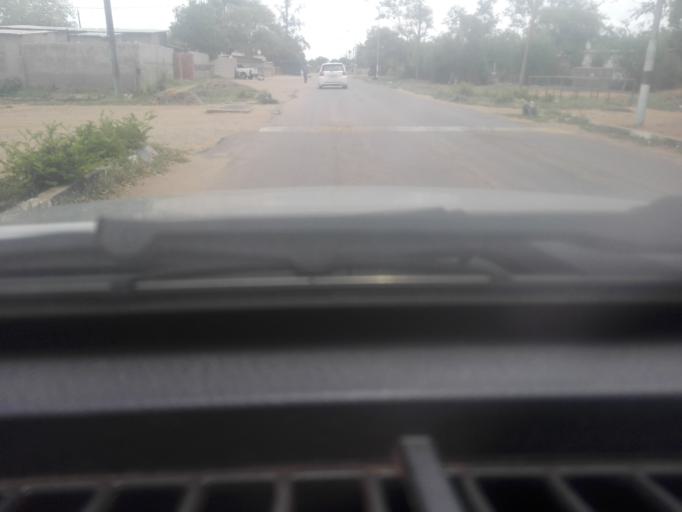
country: BW
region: South East
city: Gaborone
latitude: -24.6222
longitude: 25.9392
